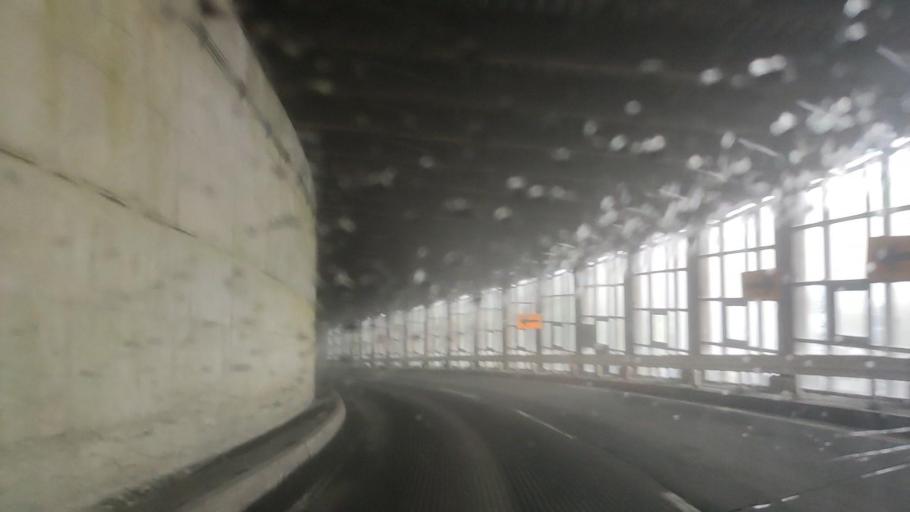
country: JP
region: Hokkaido
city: Date
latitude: 42.5492
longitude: 141.0859
